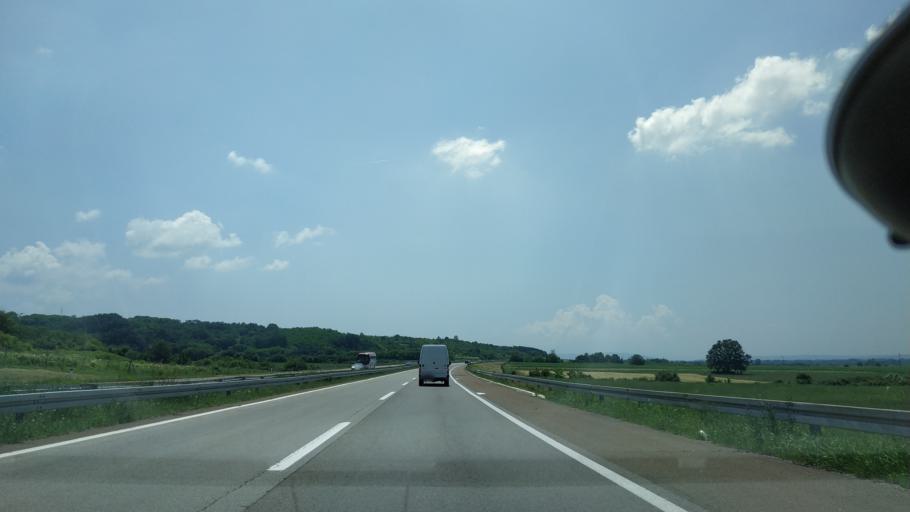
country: RS
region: Central Serbia
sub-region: Pomoravski Okrug
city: Paracin
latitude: 43.8308
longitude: 21.4279
